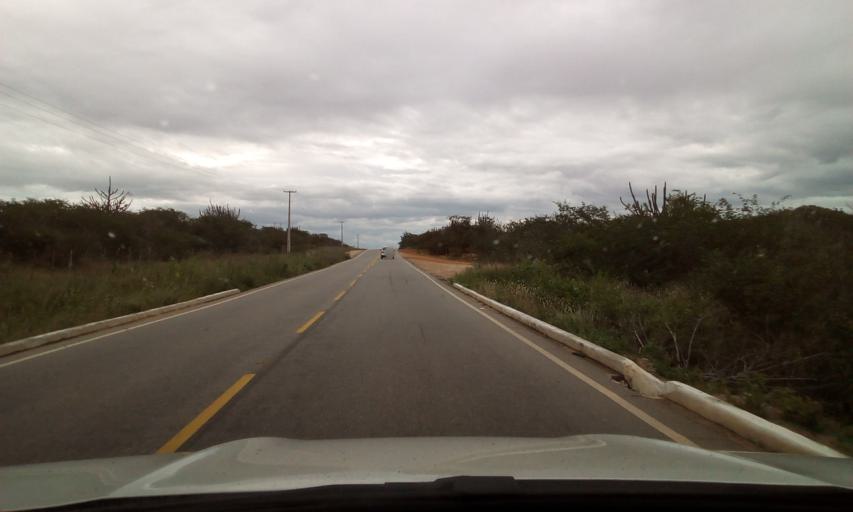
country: BR
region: Paraiba
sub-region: Picui
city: Picui
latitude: -6.5633
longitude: -36.2809
